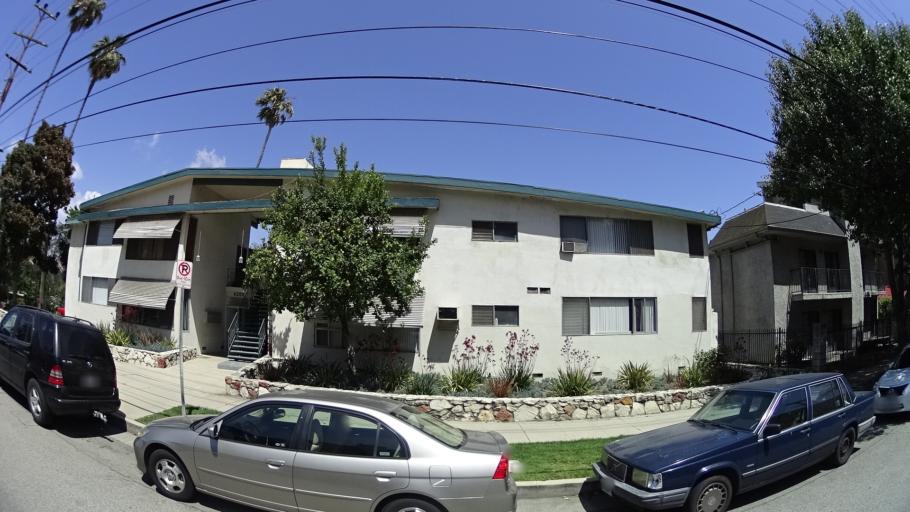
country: US
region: California
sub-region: Los Angeles County
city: Sherman Oaks
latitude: 34.1484
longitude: -118.4225
